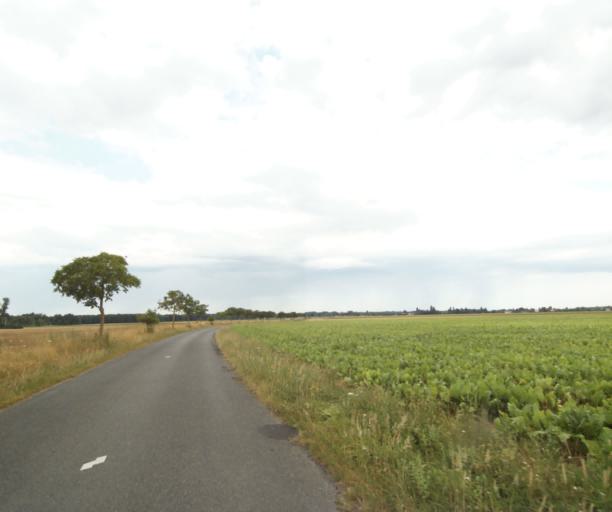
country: FR
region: Ile-de-France
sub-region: Departement de Seine-et-Marne
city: Arbonne-la-Foret
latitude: 48.4249
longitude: 2.5613
